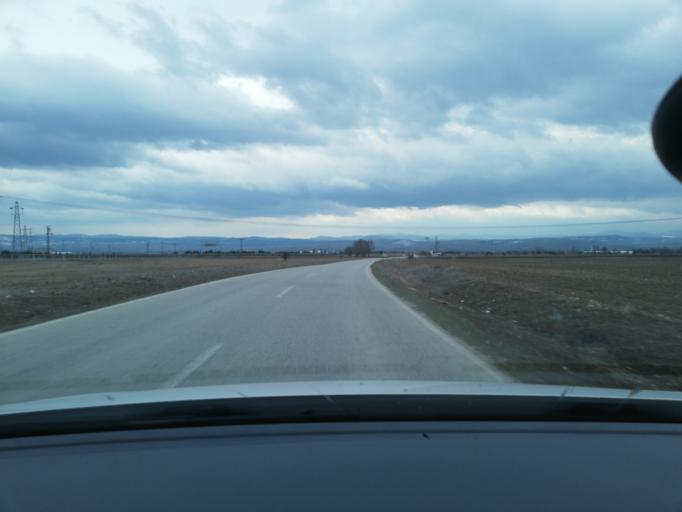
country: TR
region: Bolu
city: Gerede
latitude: 40.7779
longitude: 32.2051
